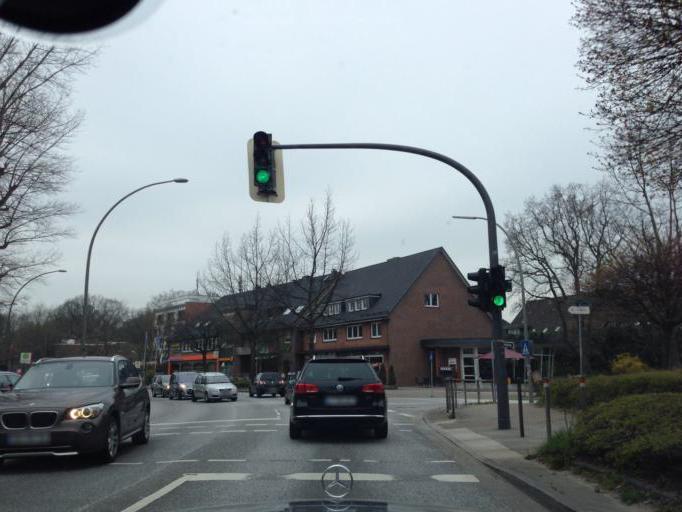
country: DE
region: Hamburg
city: Sasel
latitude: 53.6536
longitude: 10.1128
